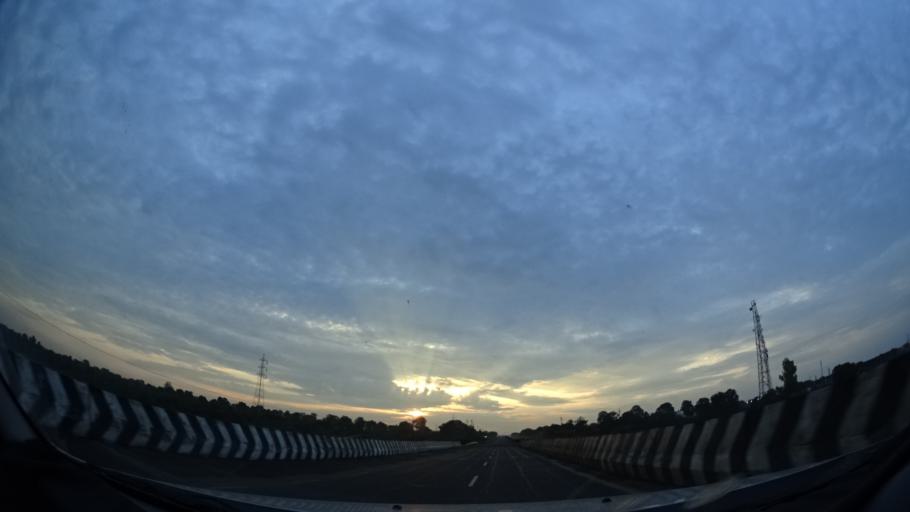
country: IN
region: Madhya Pradesh
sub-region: Sehore
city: Jawar
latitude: 22.9812
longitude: 76.3446
